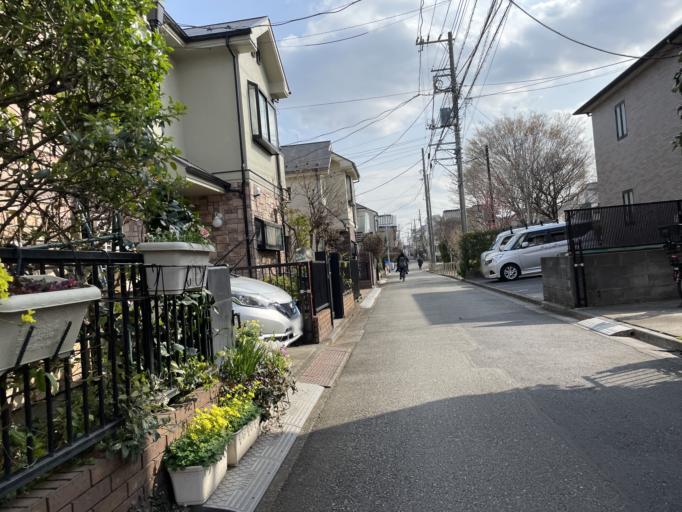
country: JP
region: Tokyo
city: Kamirenjaku
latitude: 35.6978
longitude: 139.5528
